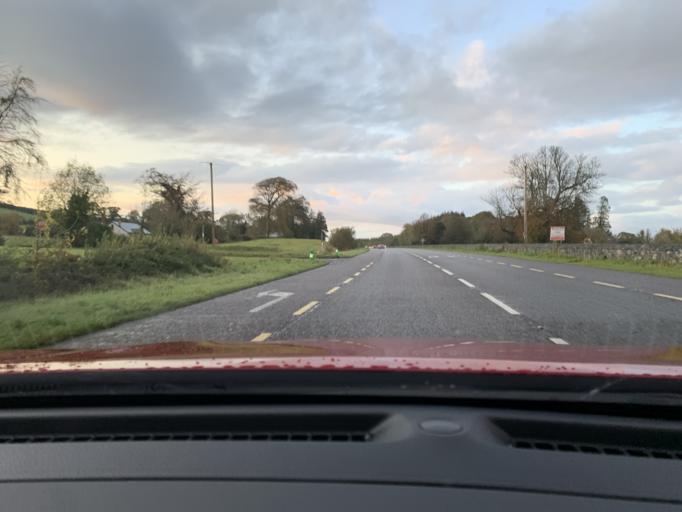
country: IE
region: Connaught
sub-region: Roscommon
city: Boyle
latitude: 54.0549
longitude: -8.3428
